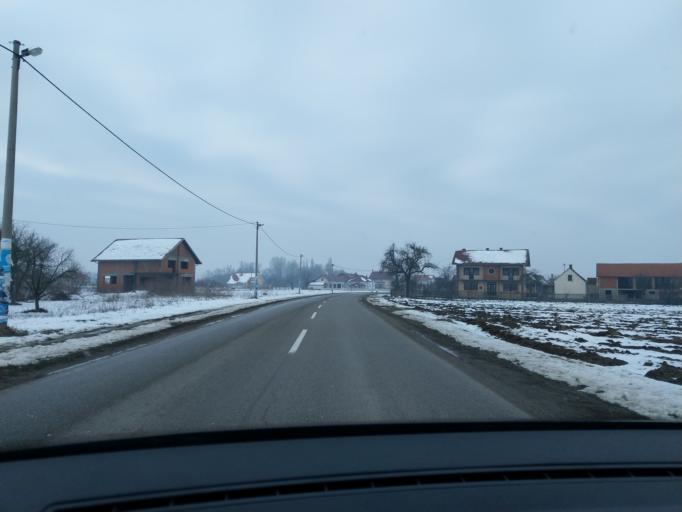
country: BA
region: Republika Srpska
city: Velika Obarska
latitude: 44.7886
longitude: 19.1840
